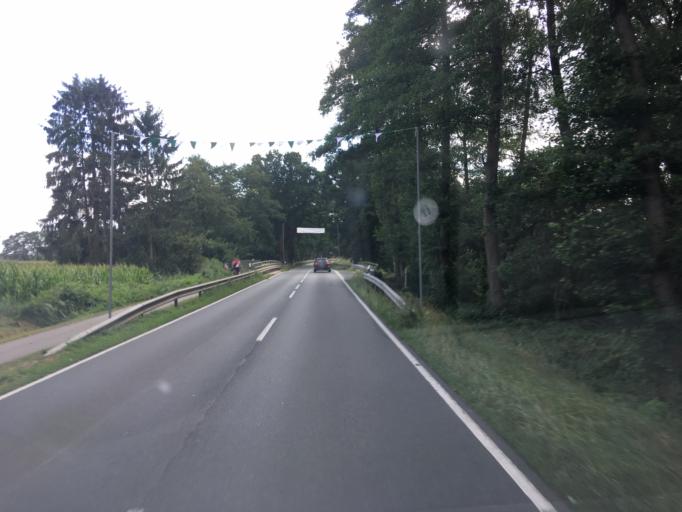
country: DE
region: Lower Saxony
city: Friesoythe
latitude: 53.0699
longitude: 7.8469
